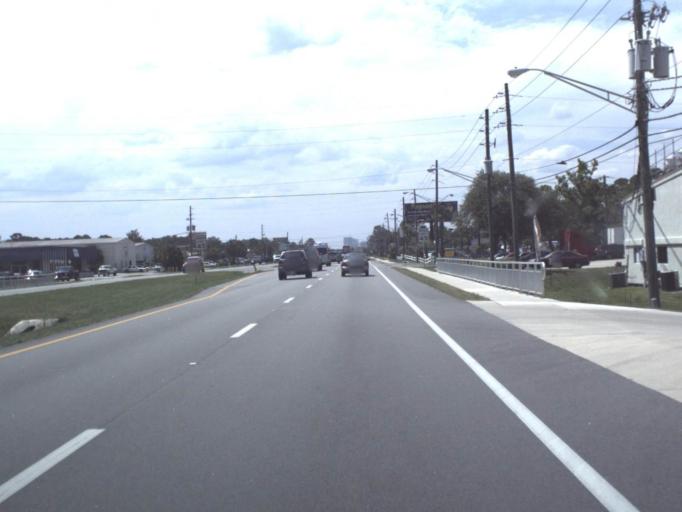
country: US
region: Florida
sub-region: Duval County
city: Jacksonville
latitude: 30.2698
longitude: -81.6208
